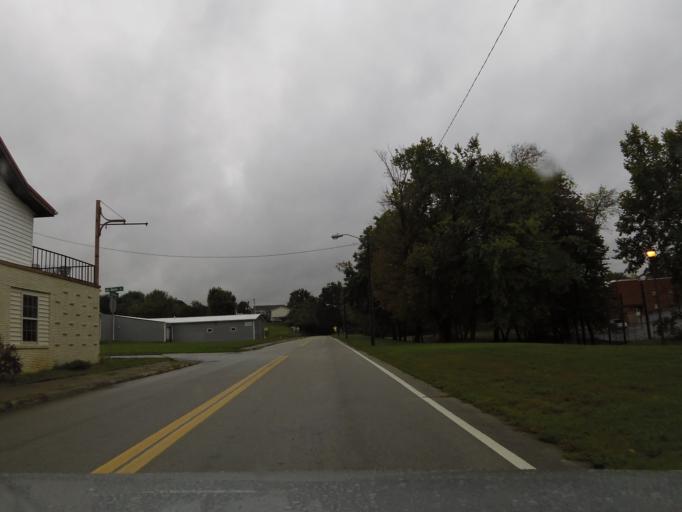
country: US
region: Tennessee
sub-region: Blount County
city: Maryville
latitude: 35.7649
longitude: -83.9692
